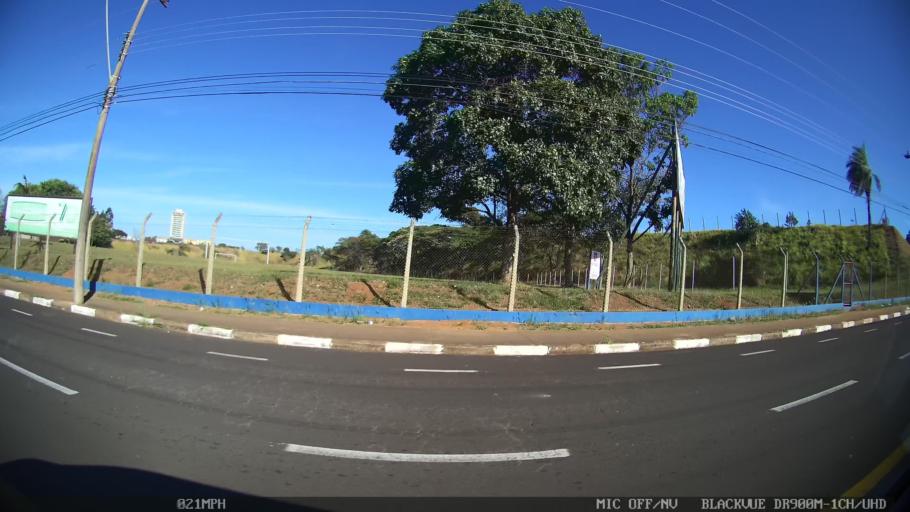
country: BR
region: Sao Paulo
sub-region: Franca
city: Franca
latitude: -20.5429
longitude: -47.4132
